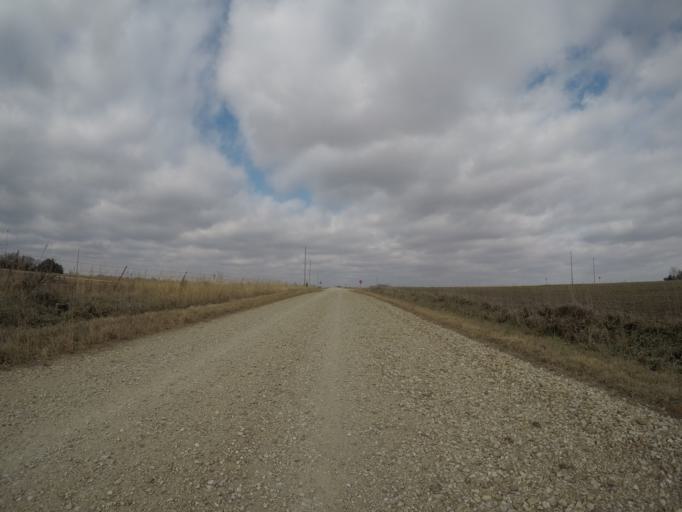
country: US
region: Kansas
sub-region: Morris County
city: Council Grove
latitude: 38.7965
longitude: -96.3529
